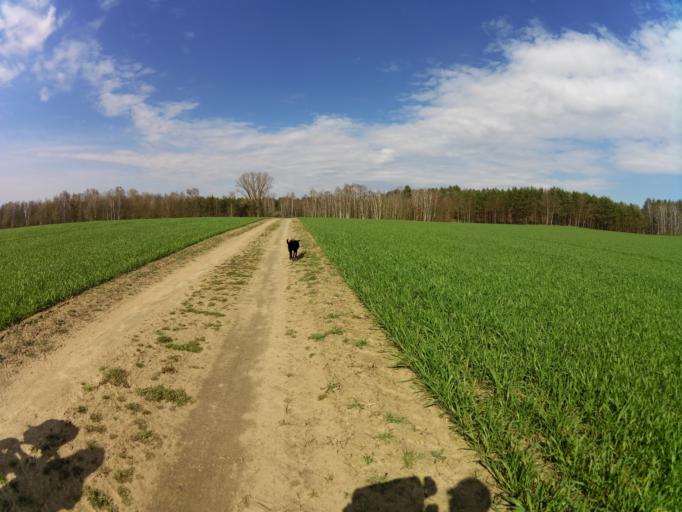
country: PL
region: West Pomeranian Voivodeship
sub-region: Powiat mysliborski
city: Mysliborz
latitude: 52.9430
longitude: 14.8629
